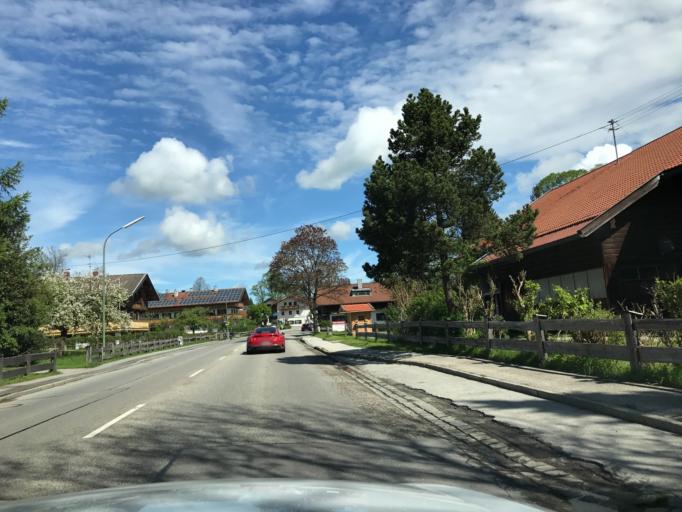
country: DE
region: Bavaria
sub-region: Upper Bavaria
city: Gmund am Tegernsee
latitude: 47.7567
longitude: 11.7361
